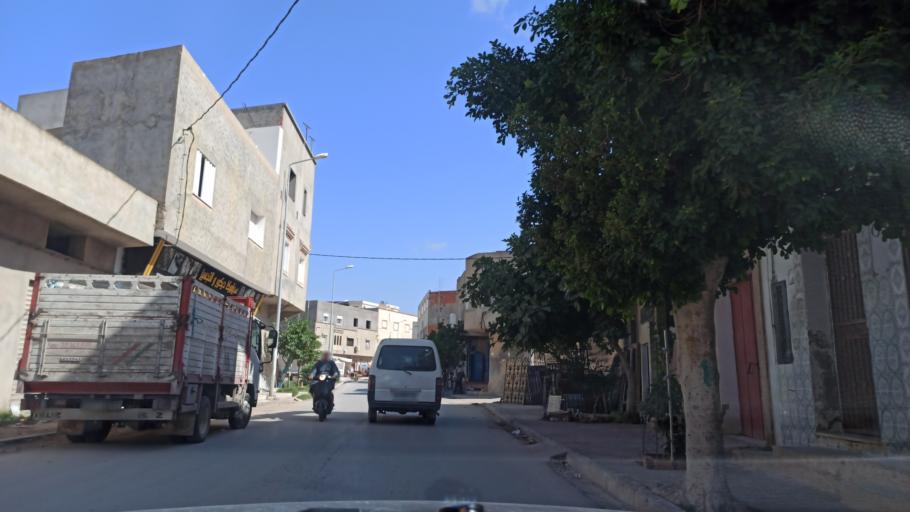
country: TN
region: Nabul
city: Nabeul
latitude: 36.4665
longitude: 10.7388
